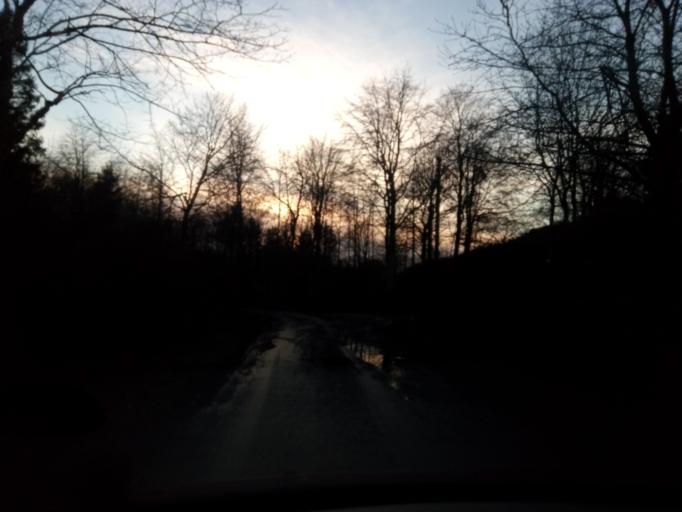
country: GB
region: Scotland
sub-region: The Scottish Borders
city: Saint Boswells
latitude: 55.5150
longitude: -2.6619
